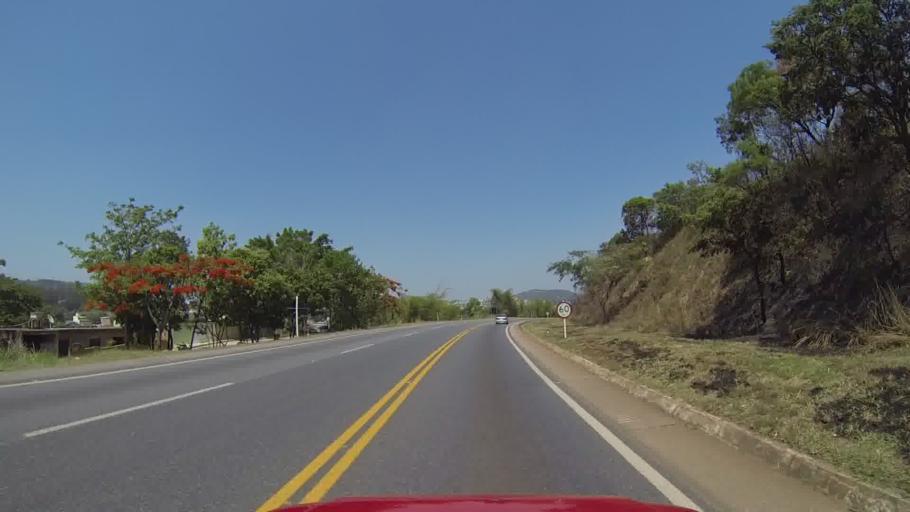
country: BR
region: Minas Gerais
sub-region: Itauna
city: Itauna
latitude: -20.0621
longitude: -44.5555
